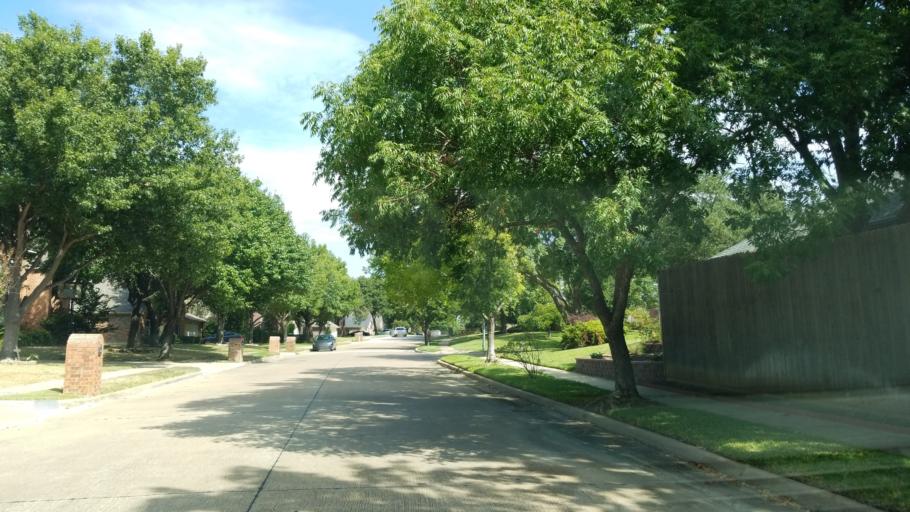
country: US
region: Texas
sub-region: Tarrant County
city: Euless
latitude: 32.8851
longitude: -97.0949
